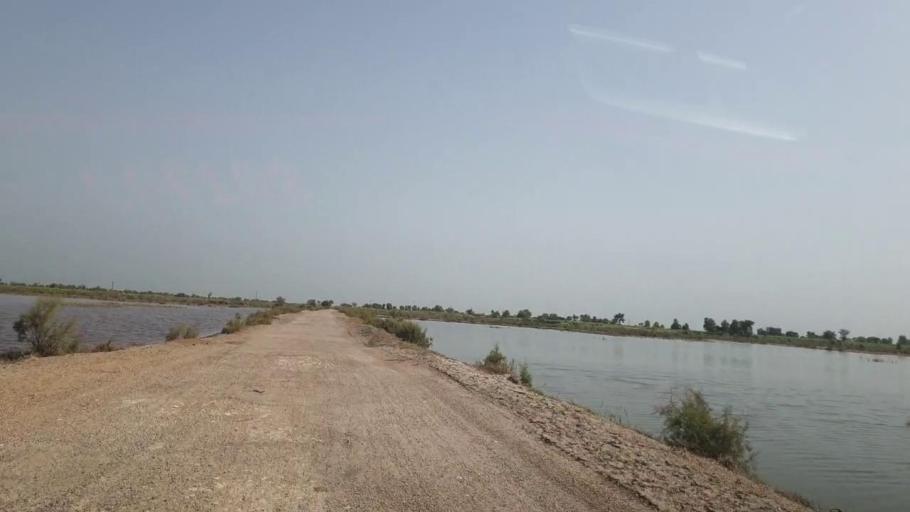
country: PK
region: Sindh
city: Sakrand
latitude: 26.3014
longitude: 68.2202
